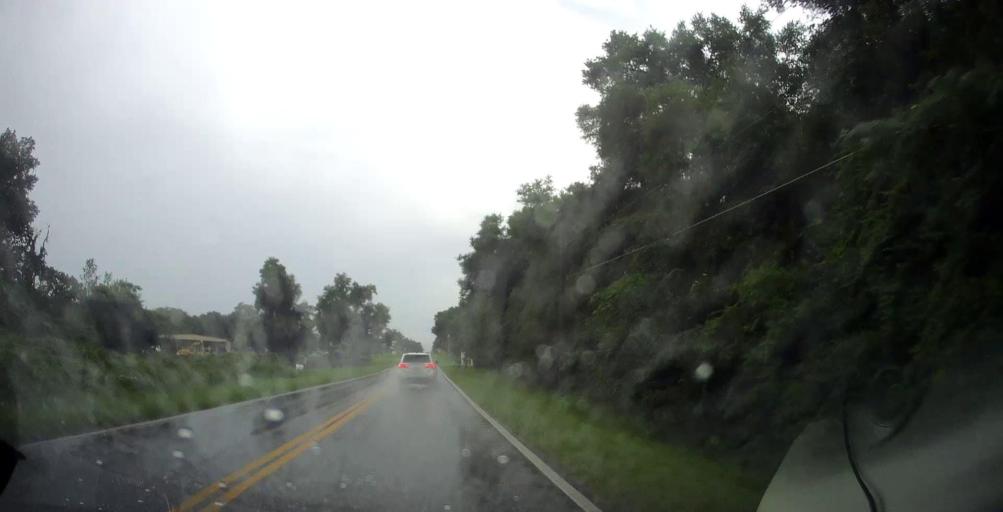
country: US
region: Florida
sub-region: Marion County
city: Ocala
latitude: 29.2401
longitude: -82.0869
